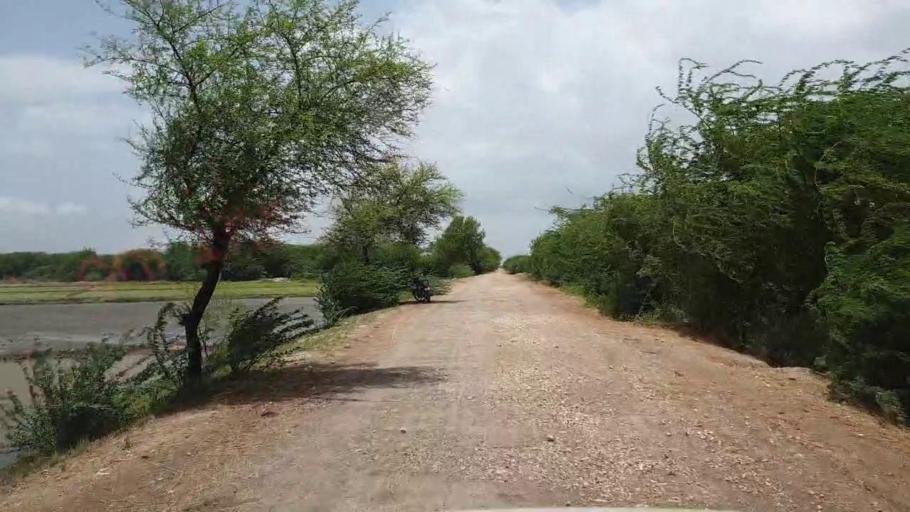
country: PK
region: Sindh
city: Kario
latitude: 24.6965
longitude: 68.6418
